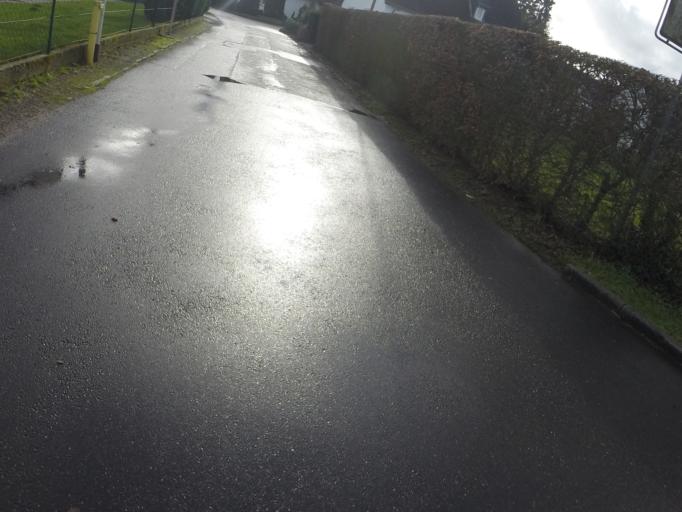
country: NL
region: Limburg
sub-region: Gemeente Kerkrade
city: Kerkrade
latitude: 50.8279
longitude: 6.0663
